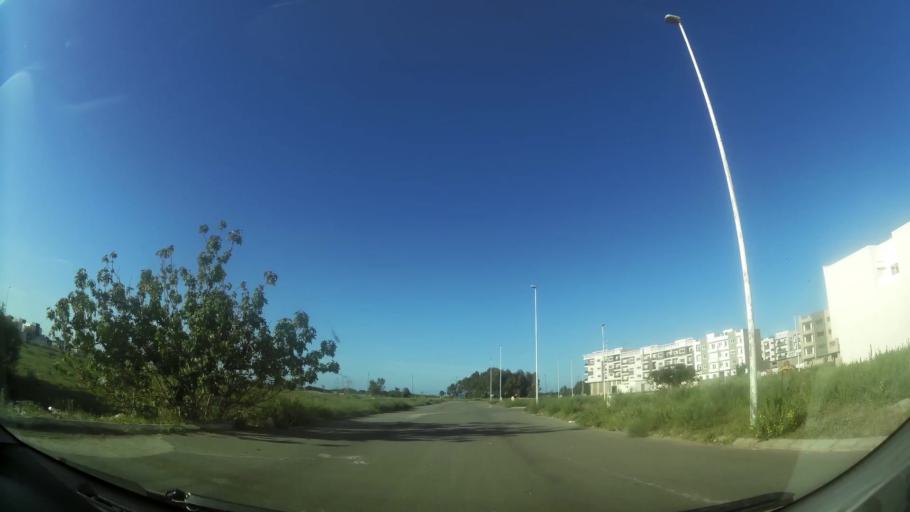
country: MA
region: Oriental
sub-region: Berkane-Taourirt
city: Madagh
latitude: 35.0923
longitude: -2.2600
